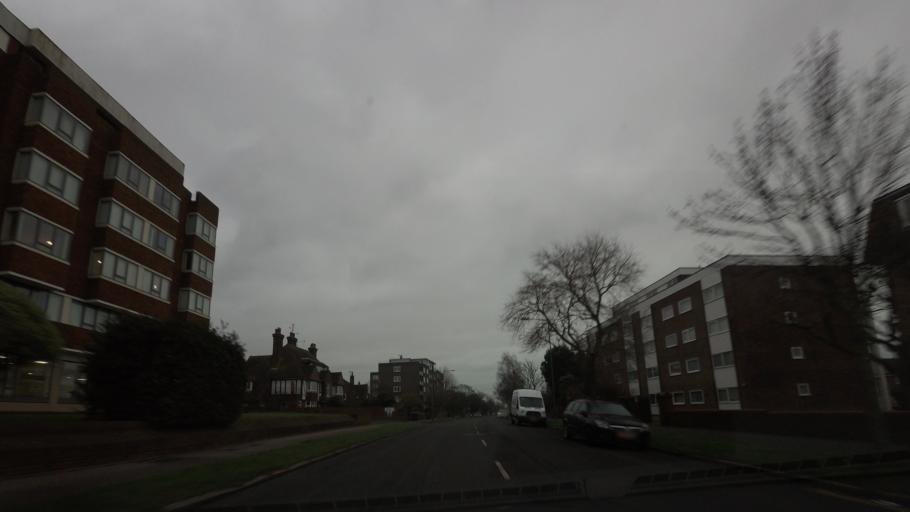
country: GB
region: England
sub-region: East Sussex
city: Bexhill-on-Sea
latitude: 50.8414
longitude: 0.4555
